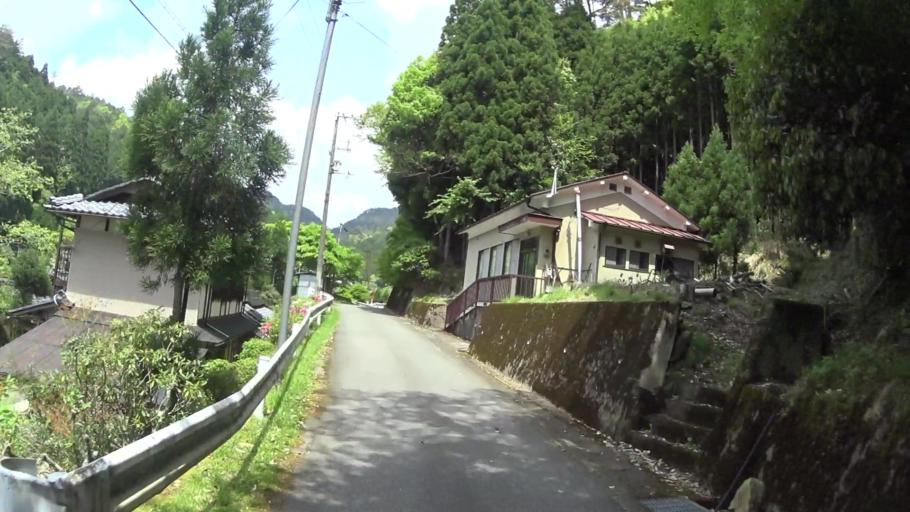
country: JP
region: Kyoto
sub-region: Kyoto-shi
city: Kamigyo-ku
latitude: 35.1223
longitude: 135.7015
